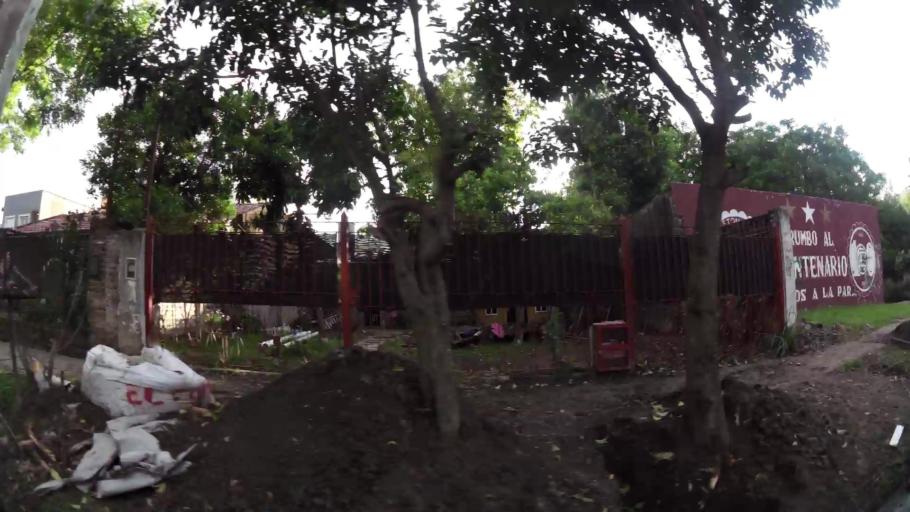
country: AR
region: Buenos Aires
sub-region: Partido de Lomas de Zamora
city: Lomas de Zamora
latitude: -34.7467
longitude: -58.3542
